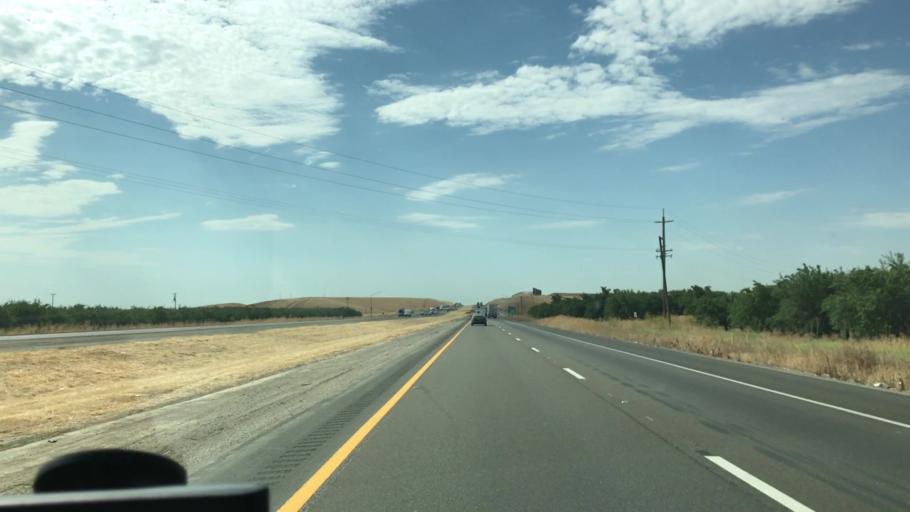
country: US
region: California
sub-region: Stanislaus County
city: Patterson
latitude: 37.4029
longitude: -121.1422
